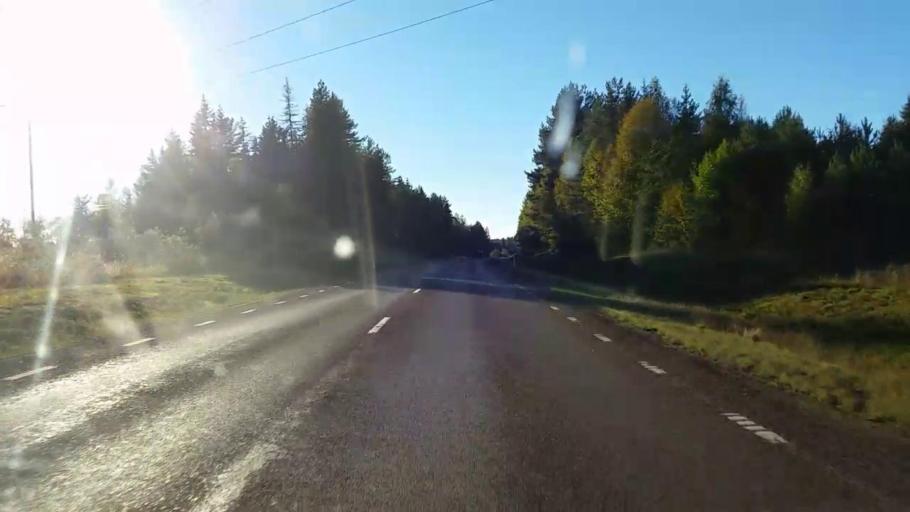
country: SE
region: Gaevleborg
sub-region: Ljusdals Kommun
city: Jaervsoe
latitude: 61.8051
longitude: 16.2609
